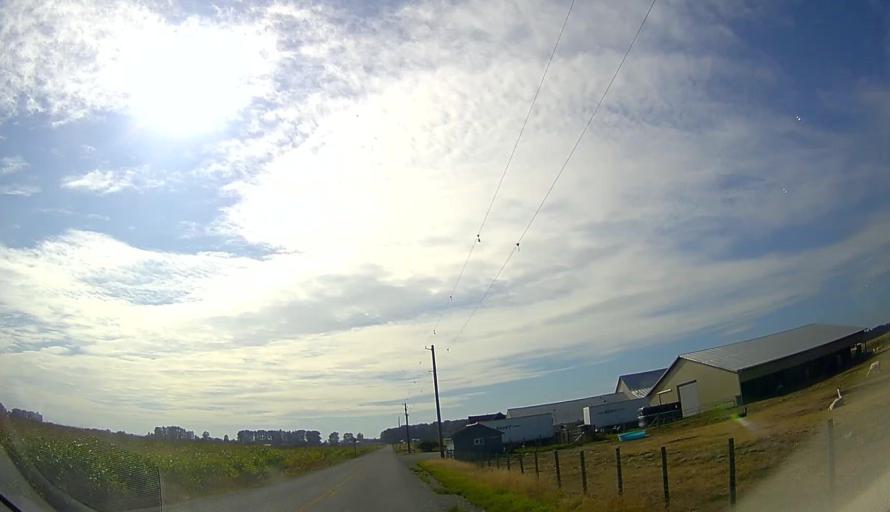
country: US
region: Washington
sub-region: Skagit County
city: Mount Vernon
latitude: 48.3703
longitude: -122.3403
